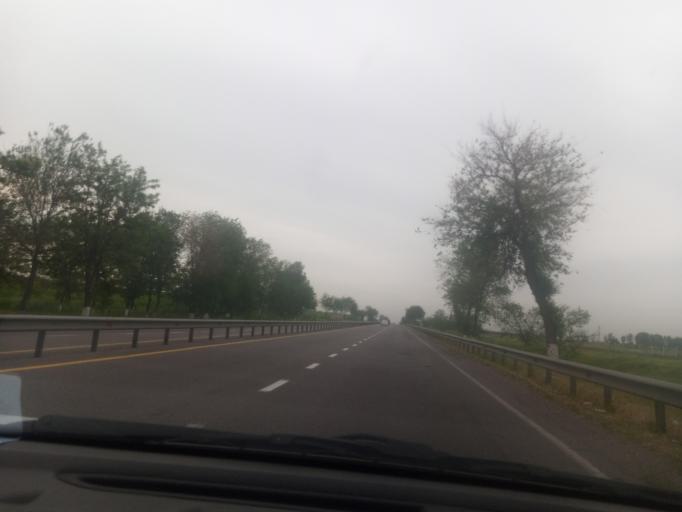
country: UZ
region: Toshkent
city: Tuytepa
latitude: 41.1043
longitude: 69.4532
